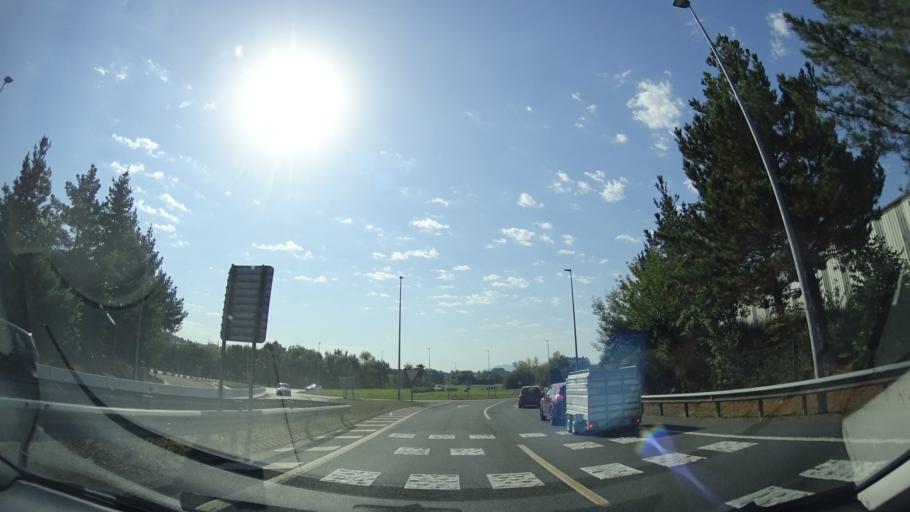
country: ES
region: Basque Country
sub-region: Bizkaia
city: Mungia
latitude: 43.3574
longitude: -2.8379
